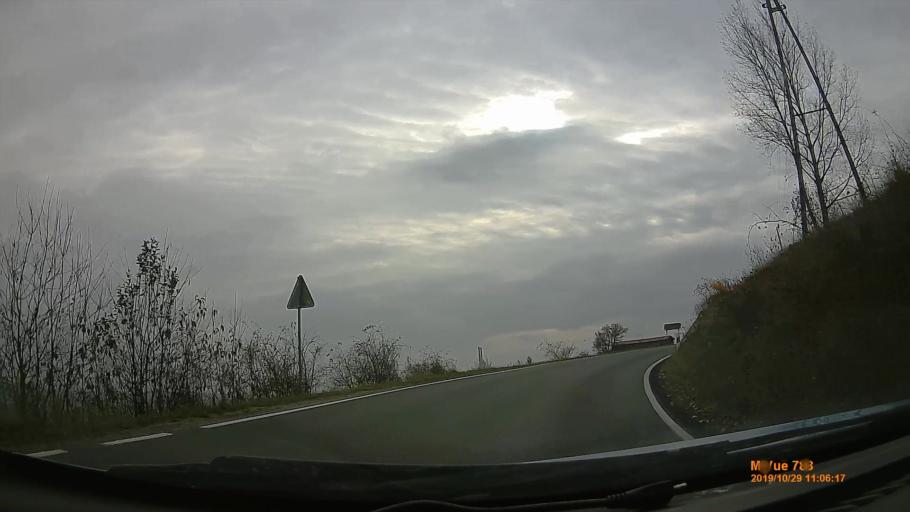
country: PL
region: Lower Silesian Voivodeship
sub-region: Powiat klodzki
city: Szczytna
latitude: 50.4651
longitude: 16.4811
